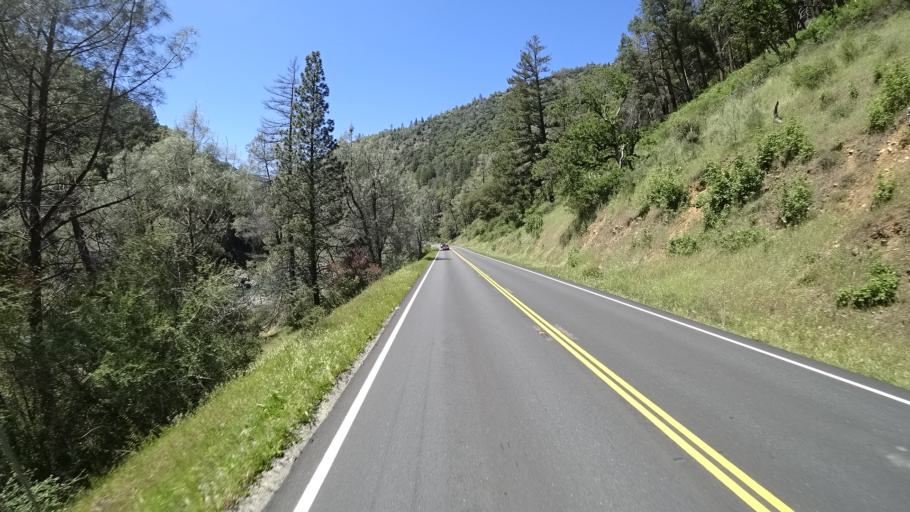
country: US
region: California
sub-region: Humboldt County
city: Willow Creek
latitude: 40.7900
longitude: -123.4335
